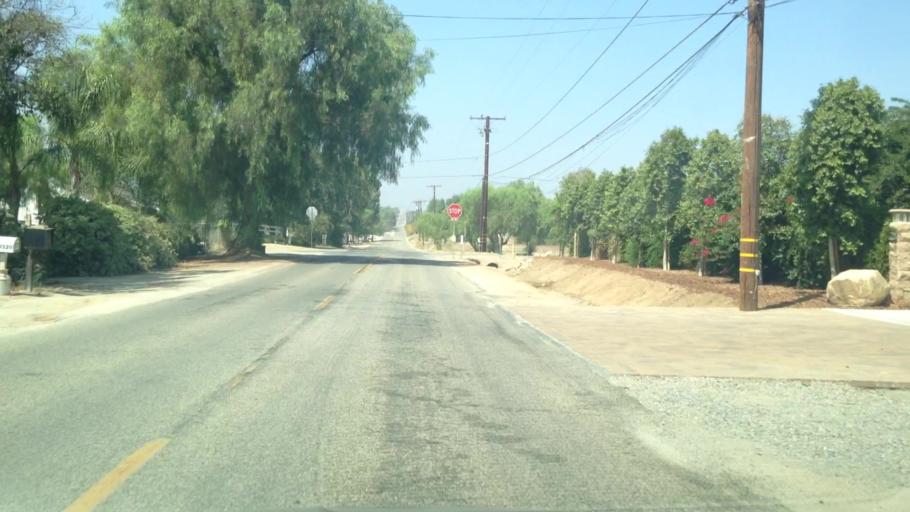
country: US
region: California
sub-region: Riverside County
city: Woodcrest
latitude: 33.8729
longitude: -117.3218
